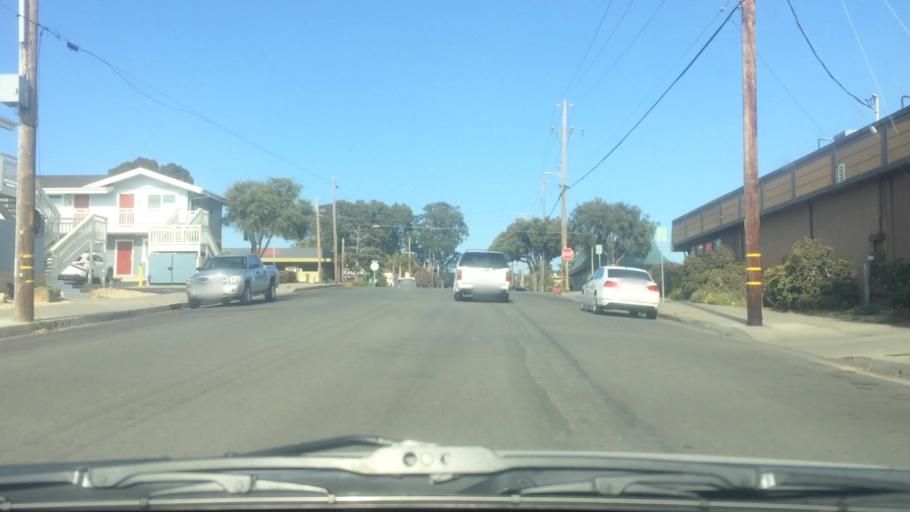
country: US
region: California
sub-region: San Luis Obispo County
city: Morro Bay
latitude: 35.3678
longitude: -120.8508
